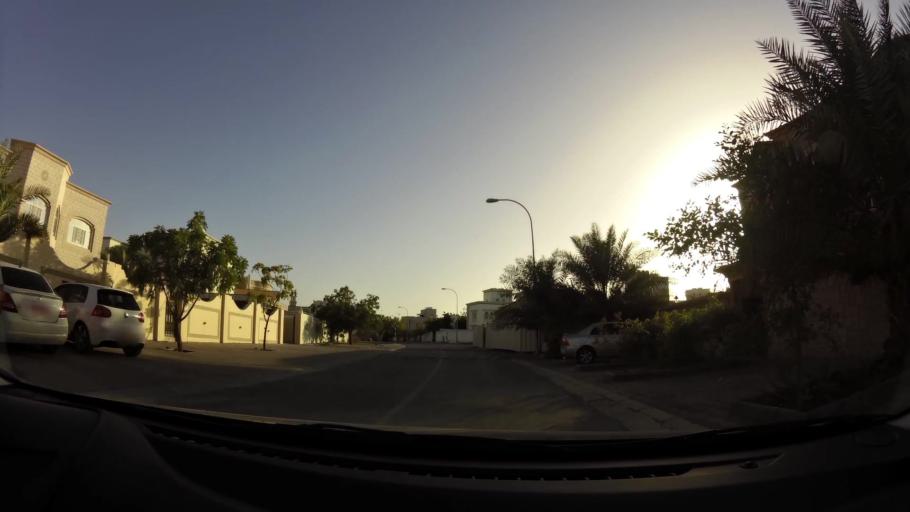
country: OM
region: Muhafazat Masqat
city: As Sib al Jadidah
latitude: 23.6083
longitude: 58.2280
